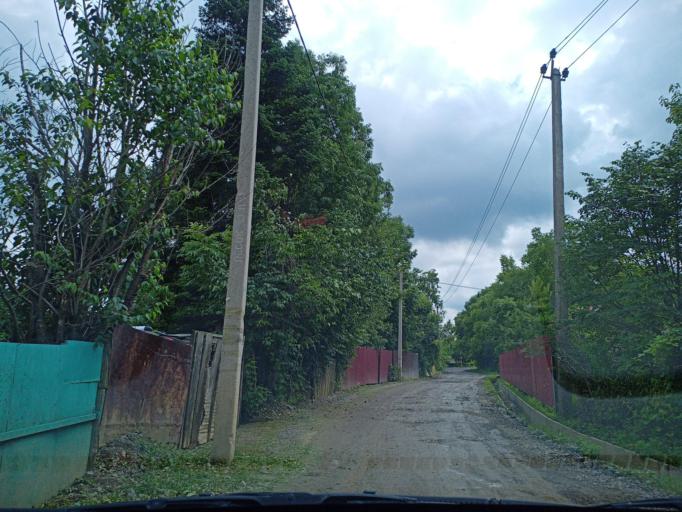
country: RU
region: Khabarovsk Krai
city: Korfovskiy
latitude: 48.3199
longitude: 135.1049
